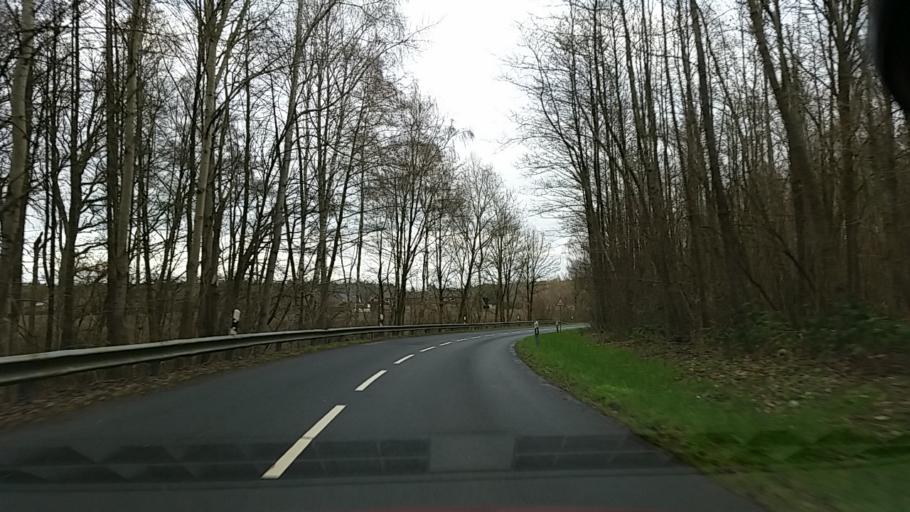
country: DE
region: Lower Saxony
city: Bodenteich
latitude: 52.8330
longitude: 10.6653
